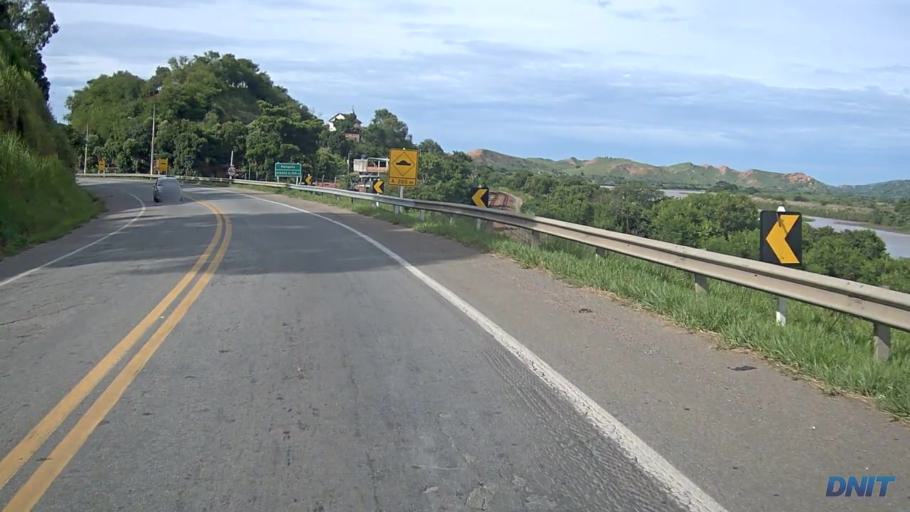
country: BR
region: Minas Gerais
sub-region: Belo Oriente
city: Belo Oriente
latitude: -19.1595
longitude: -42.2381
